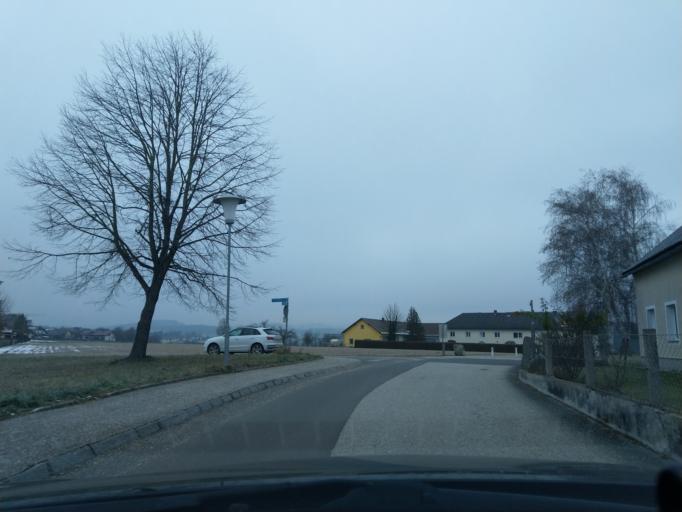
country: AT
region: Upper Austria
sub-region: Politischer Bezirk Urfahr-Umgebung
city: Engerwitzdorf
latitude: 48.3682
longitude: 14.5213
